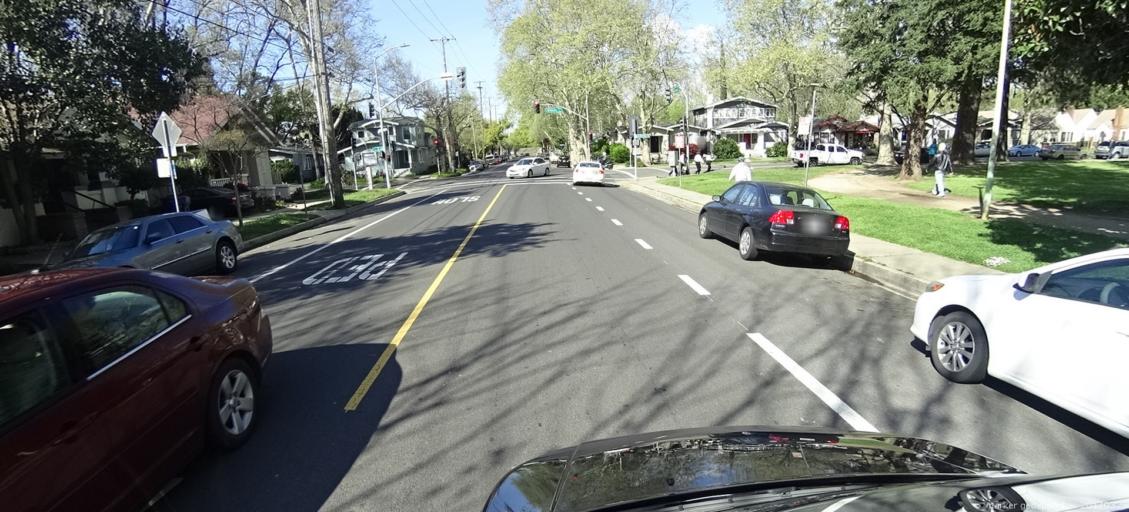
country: US
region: California
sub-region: Sacramento County
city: Sacramento
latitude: 38.5778
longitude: -121.4631
